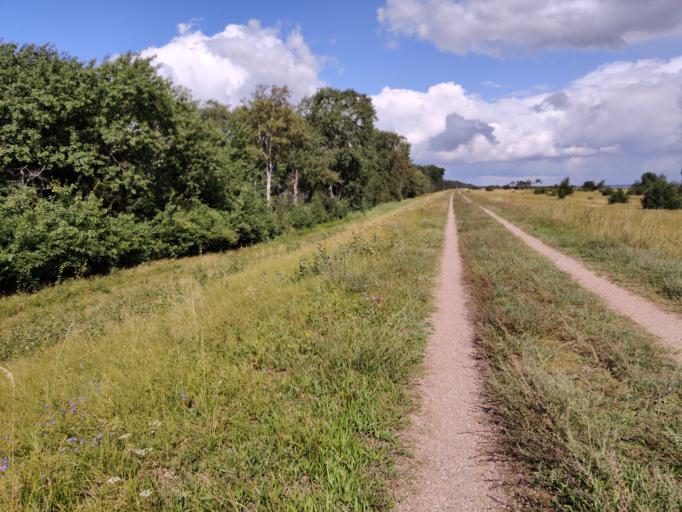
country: DK
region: Zealand
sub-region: Guldborgsund Kommune
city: Nykobing Falster
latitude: 54.6172
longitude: 11.9638
